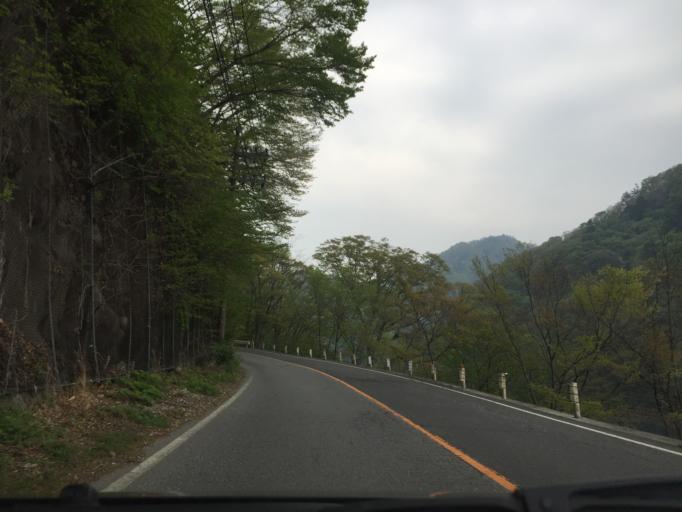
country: JP
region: Tochigi
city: Nikko
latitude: 36.9050
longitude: 139.7024
